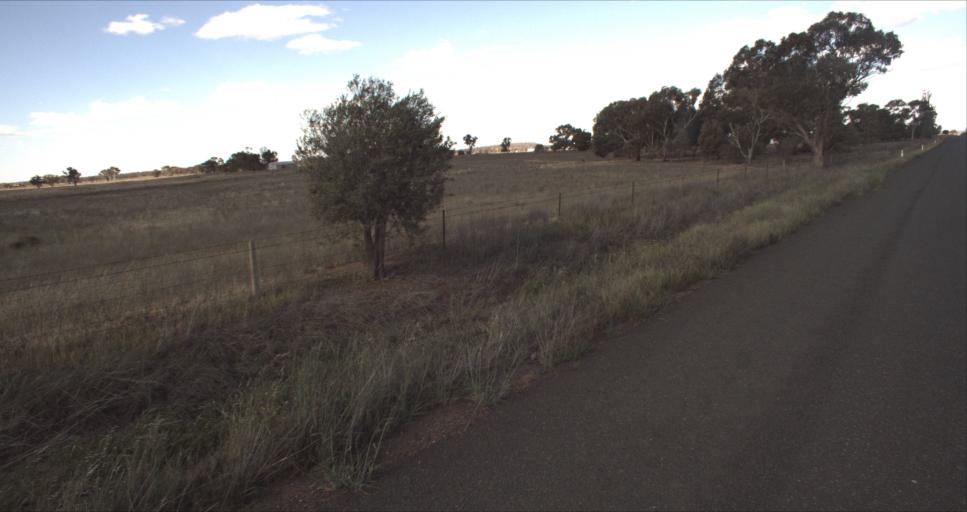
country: AU
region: New South Wales
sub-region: Griffith
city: Griffith
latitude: -34.4379
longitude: 146.2052
